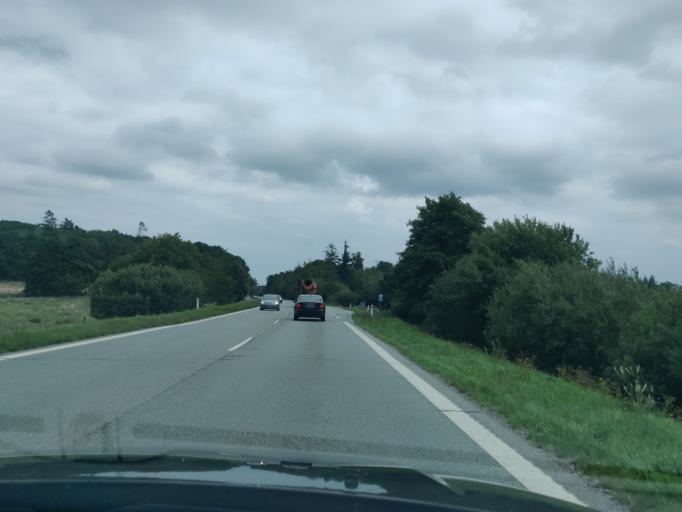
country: DK
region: North Denmark
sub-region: Alborg Kommune
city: Frejlev
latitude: 57.0102
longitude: 9.7823
